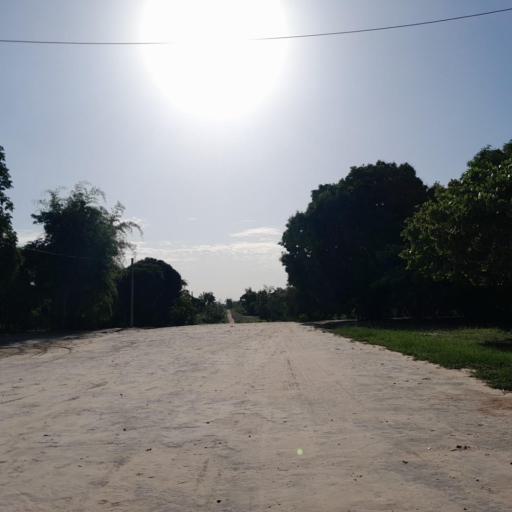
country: PE
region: Ucayali
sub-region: Provincia de Coronel Portillo
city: Puerto Callao
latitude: -8.2751
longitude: -74.6516
